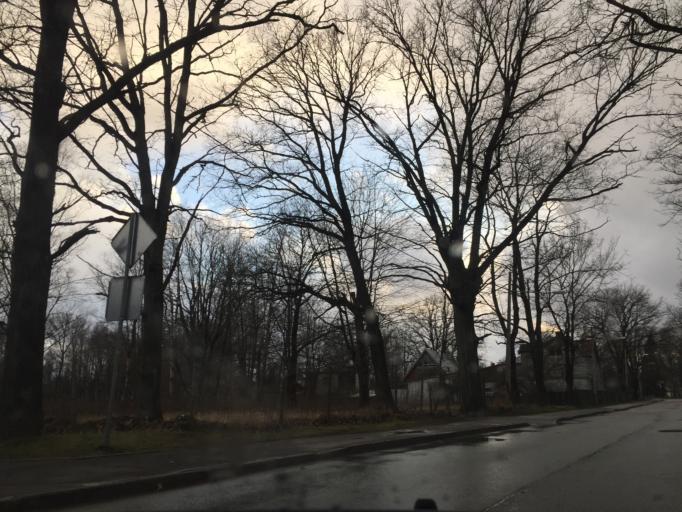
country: LV
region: Marupe
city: Marupe
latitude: 56.9322
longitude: 24.0558
